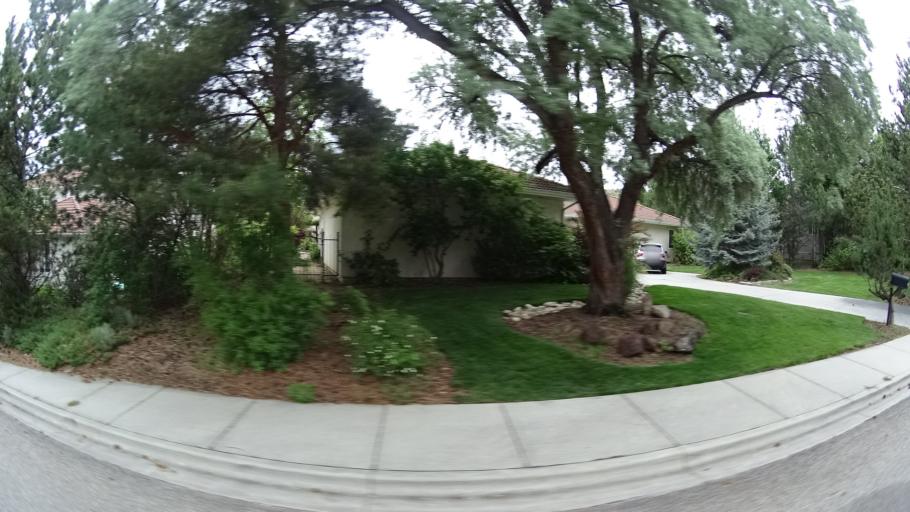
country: US
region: Idaho
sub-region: Ada County
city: Boise
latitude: 43.6124
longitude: -116.1565
